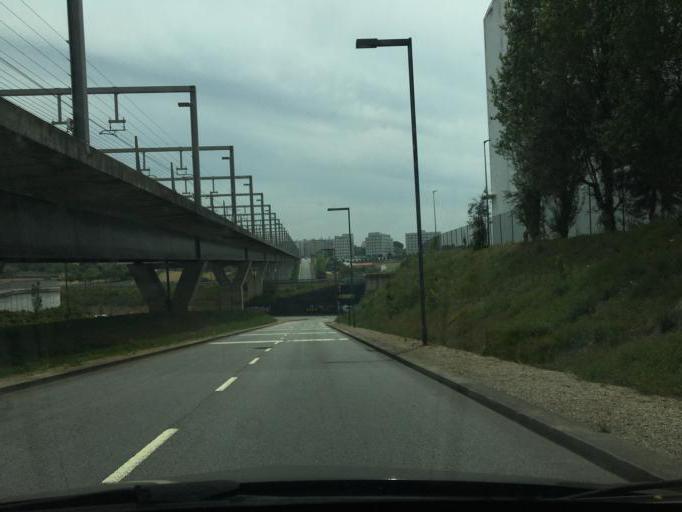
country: PT
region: Porto
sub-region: Maia
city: Maia
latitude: 41.2431
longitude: -8.6284
